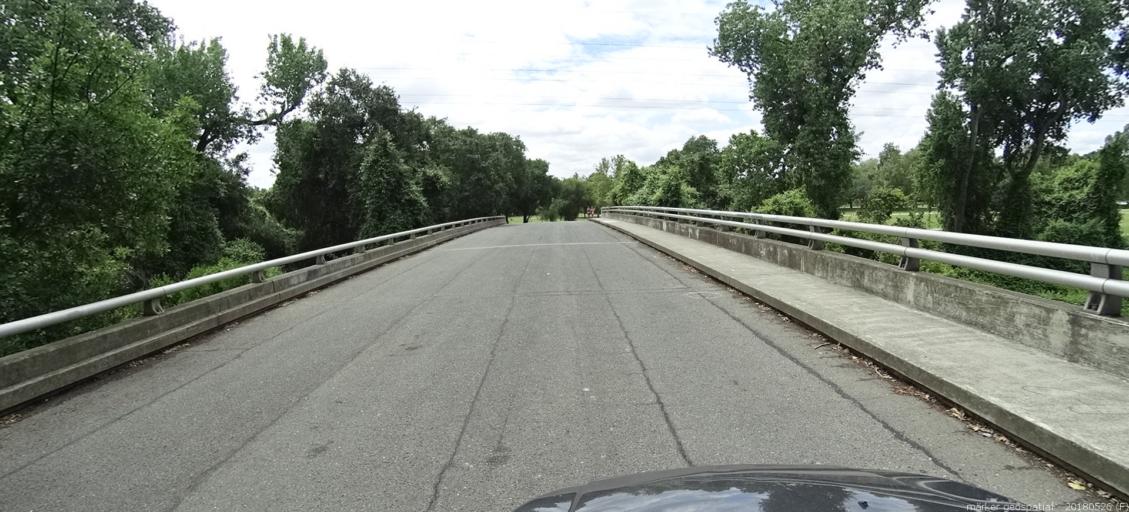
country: US
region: California
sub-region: Sacramento County
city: Sacramento
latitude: 38.6073
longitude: -121.5022
